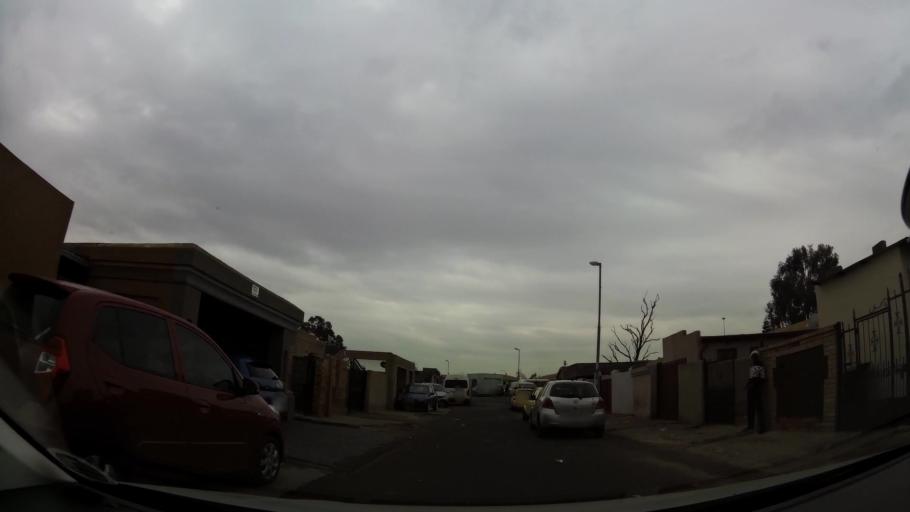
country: ZA
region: Gauteng
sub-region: City of Johannesburg Metropolitan Municipality
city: Soweto
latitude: -26.2549
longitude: 27.8761
